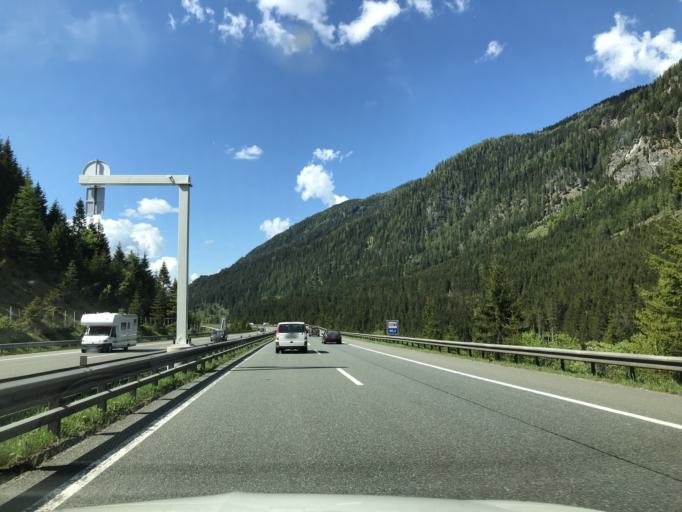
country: AT
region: Salzburg
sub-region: Politischer Bezirk Sankt Johann im Pongau
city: Flachau
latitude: 47.2743
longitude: 13.4113
